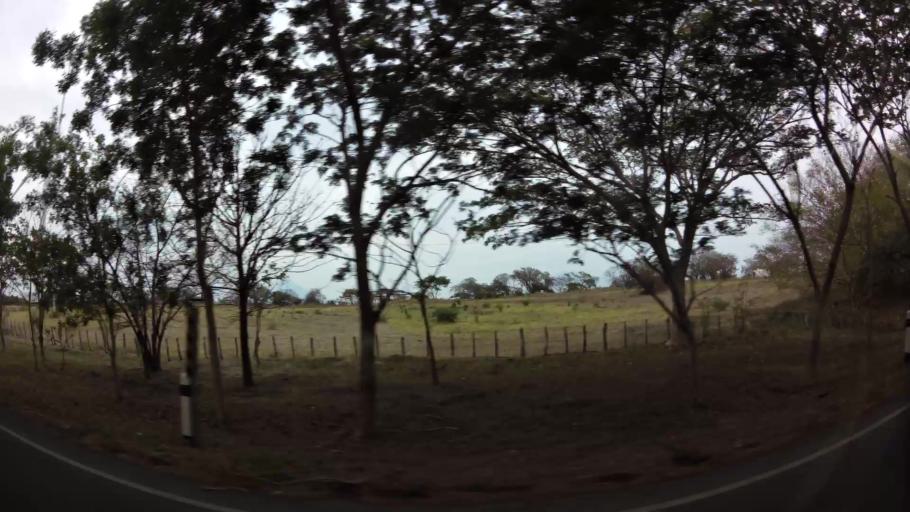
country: NI
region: Rivas
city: Rivas
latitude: 11.3343
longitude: -85.7259
